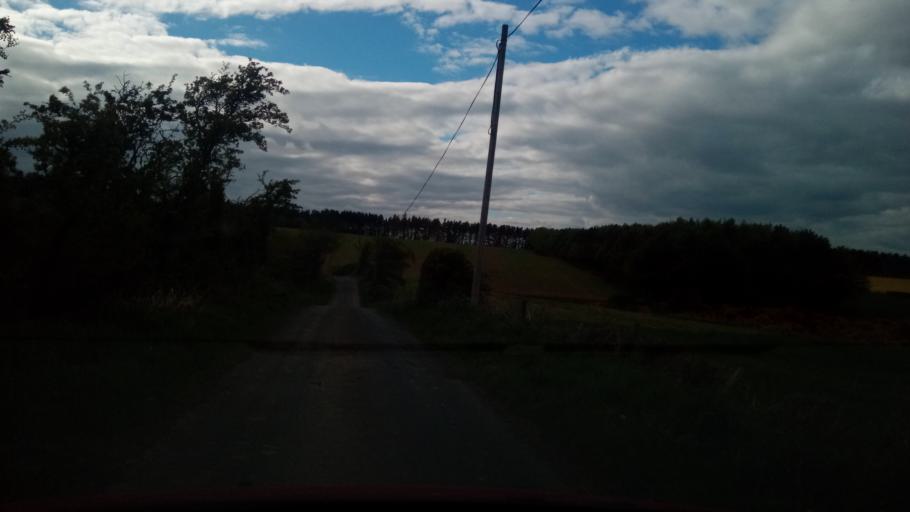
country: GB
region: Scotland
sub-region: The Scottish Borders
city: Saint Boswells
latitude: 55.5079
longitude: -2.6439
